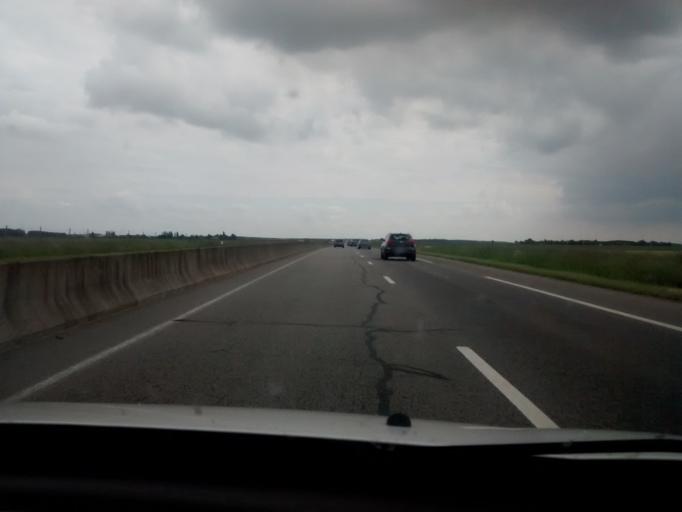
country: FR
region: Ile-de-France
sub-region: Departement des Yvelines
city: Sonchamp
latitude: 48.5987
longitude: 1.8317
